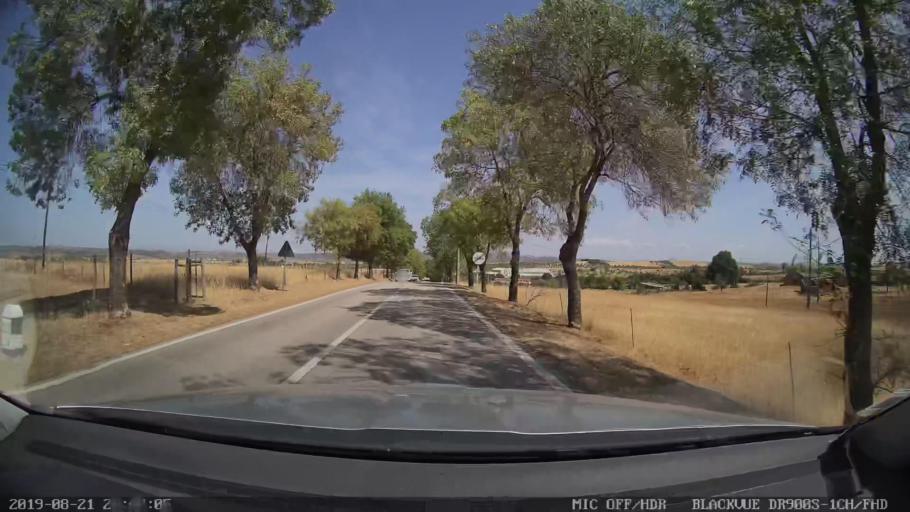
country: PT
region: Castelo Branco
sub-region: Idanha-A-Nova
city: Idanha-a-Nova
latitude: 39.8472
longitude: -7.2570
